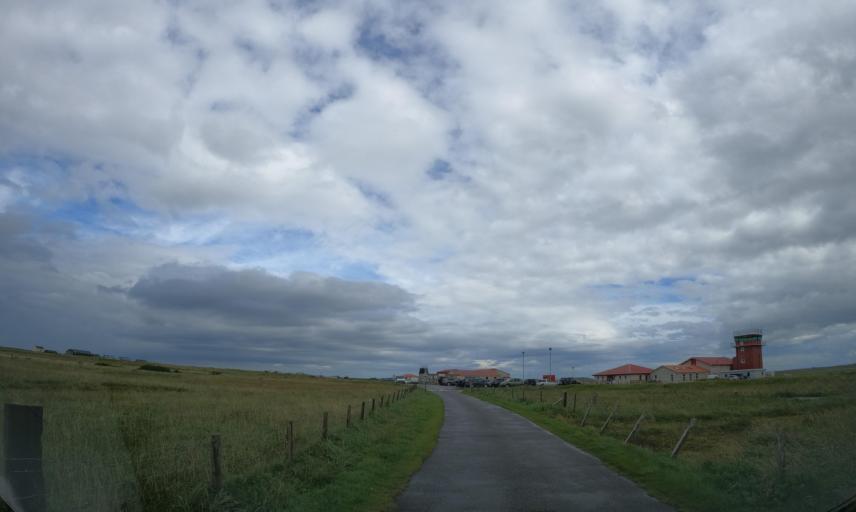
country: GB
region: Scotland
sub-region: Eilean Siar
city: Barra
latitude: 56.4979
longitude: -6.8798
